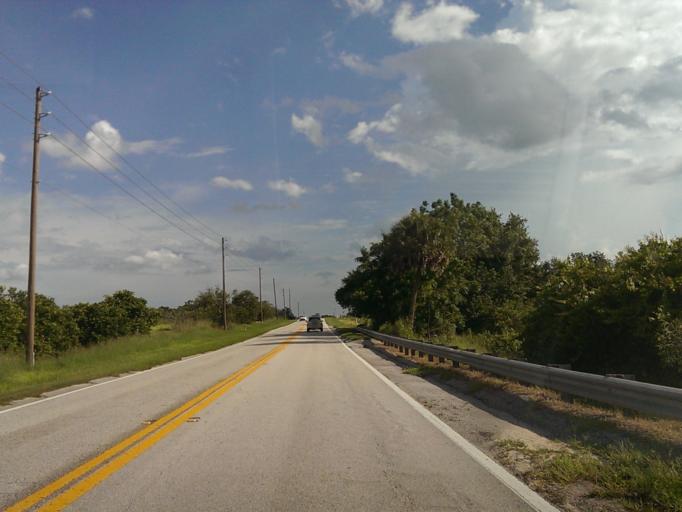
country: US
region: Florida
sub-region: Polk County
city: Citrus Ridge
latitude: 28.4147
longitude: -81.6359
